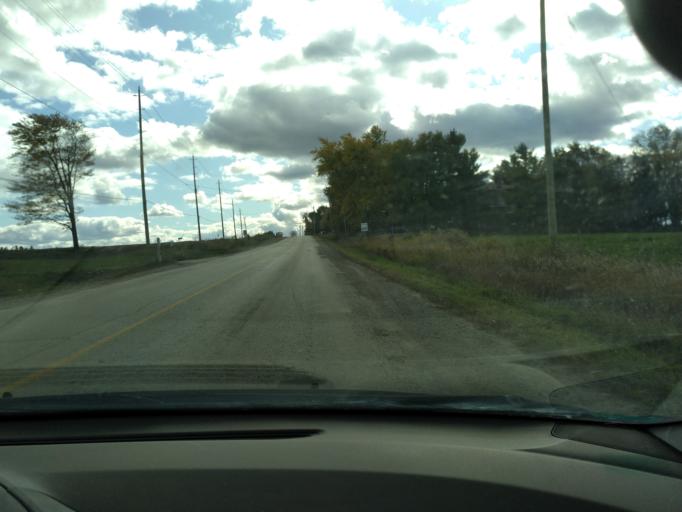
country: CA
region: Ontario
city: Bradford West Gwillimbury
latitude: 44.0883
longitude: -79.5973
